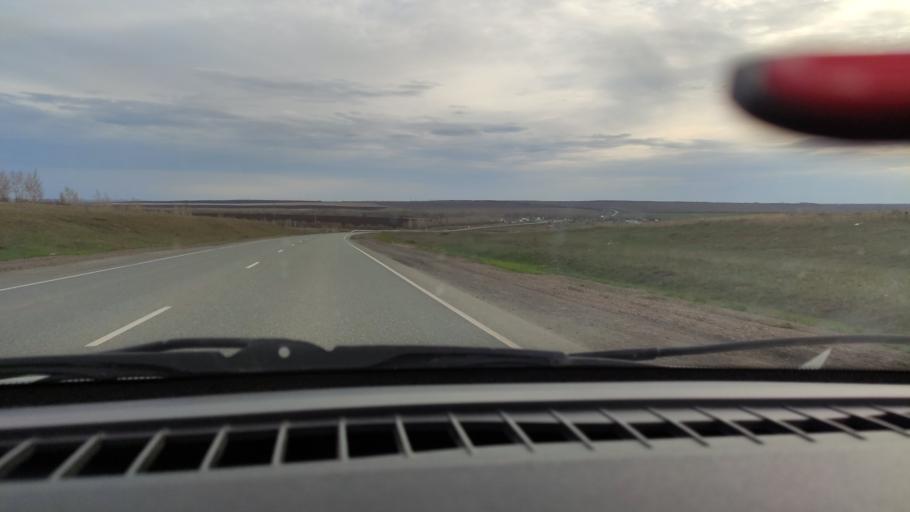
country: RU
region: Orenburg
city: Sakmara
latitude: 52.0356
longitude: 55.2470
